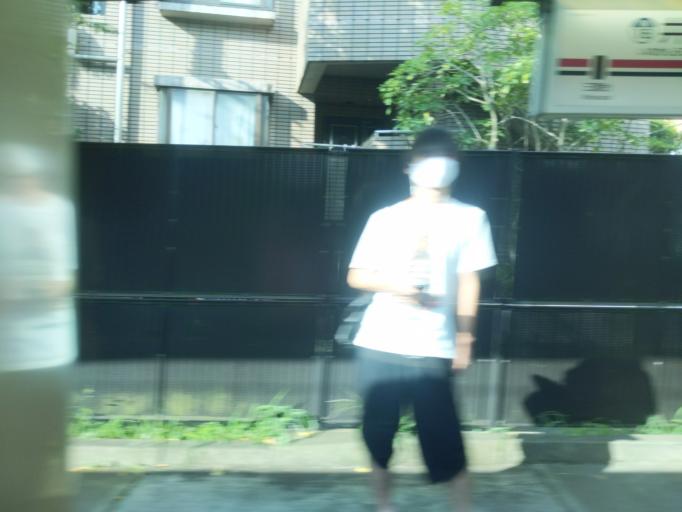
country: JP
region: Tokyo
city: Musashino
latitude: 35.6972
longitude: 139.5831
